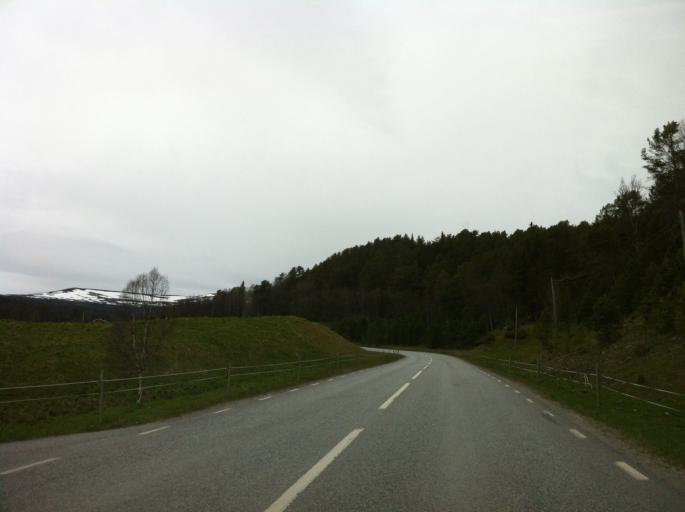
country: NO
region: Sor-Trondelag
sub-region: Tydal
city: Aas
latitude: 62.6152
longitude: 12.4906
